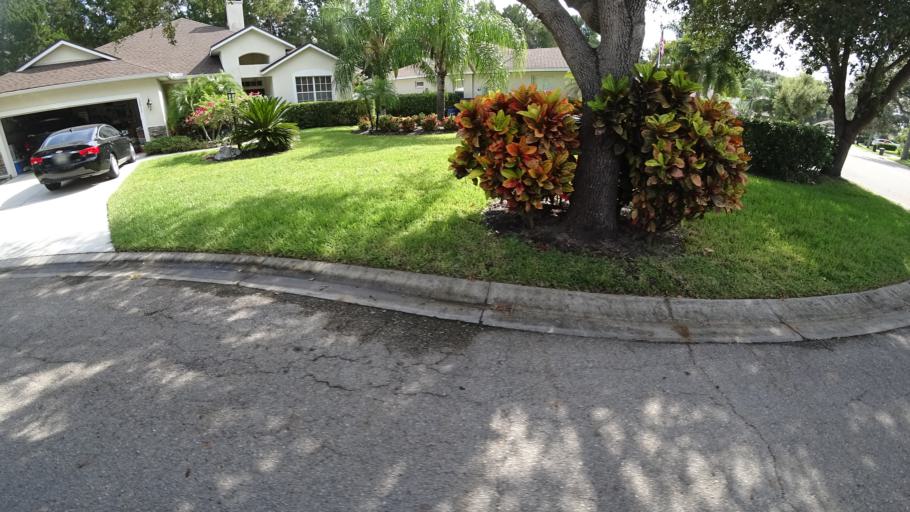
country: US
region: Florida
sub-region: Sarasota County
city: The Meadows
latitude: 27.4274
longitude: -82.4225
